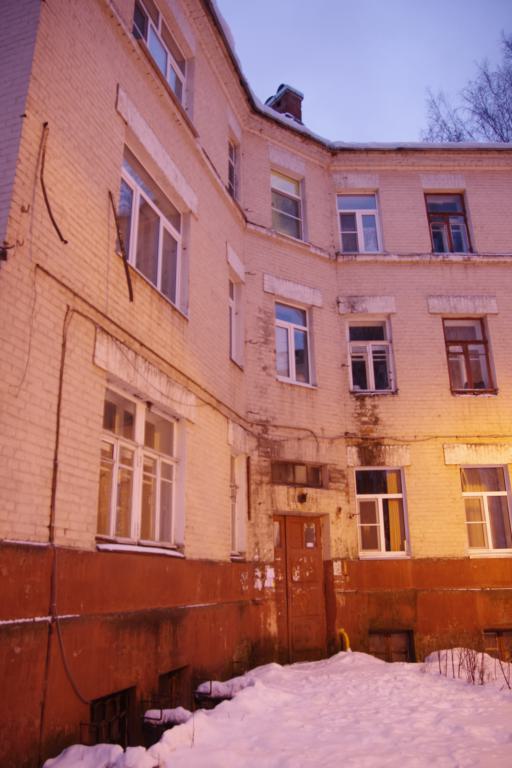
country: RU
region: Moskovskaya
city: Korolev
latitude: 55.9210
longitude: 37.8081
